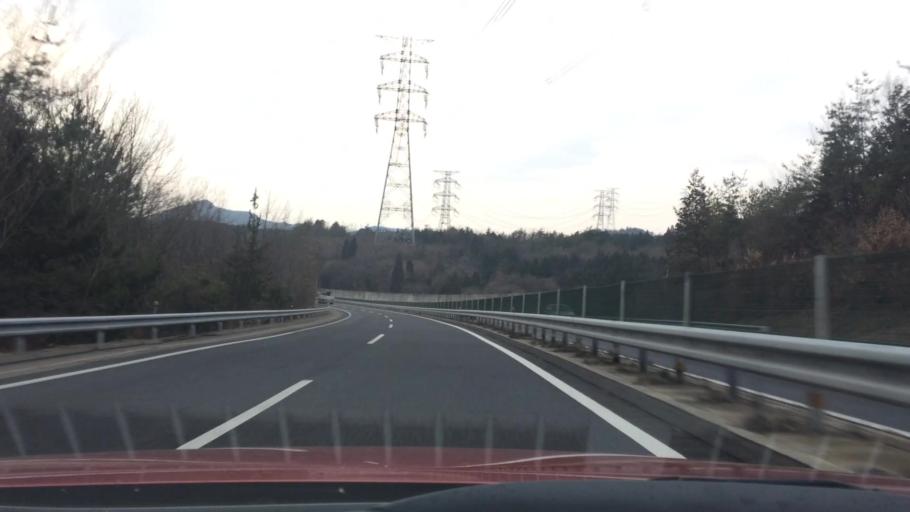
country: JP
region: Gifu
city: Mizunami
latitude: 35.4411
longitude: 137.3632
